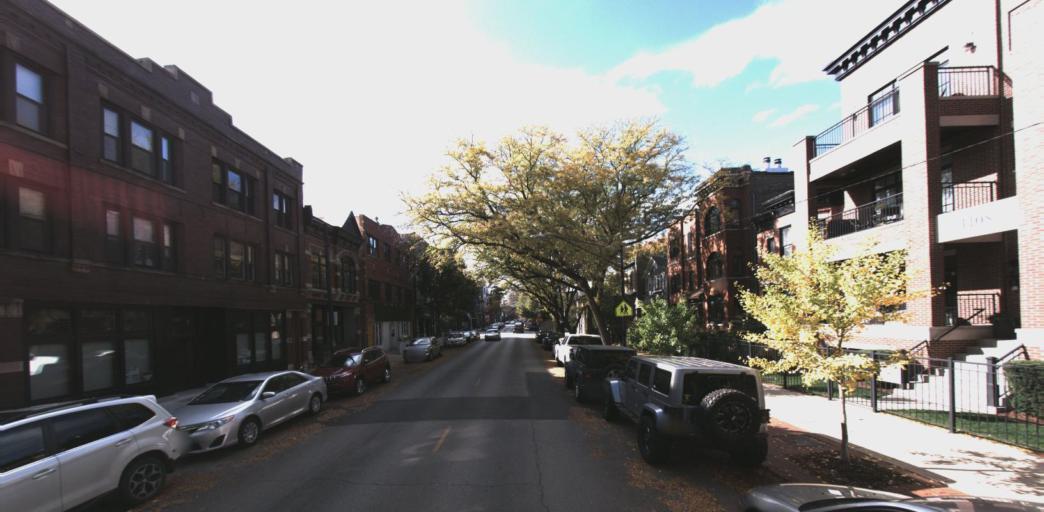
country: US
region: Illinois
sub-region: Cook County
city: Chicago
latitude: 41.9217
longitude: -87.6563
